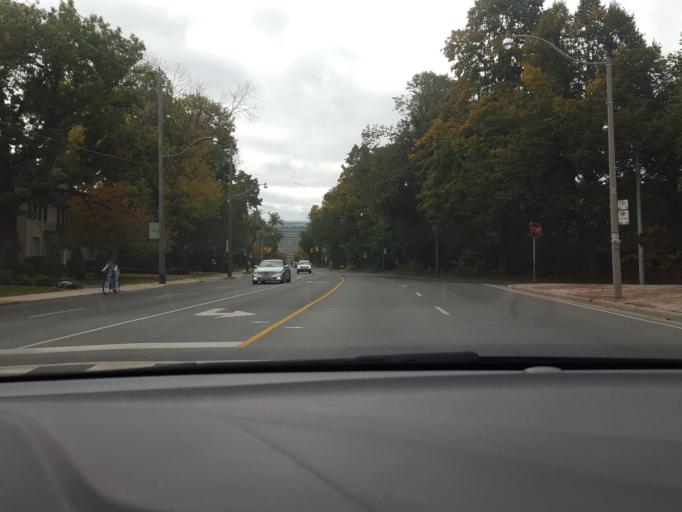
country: CA
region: Ontario
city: Toronto
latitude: 43.6954
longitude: -79.4024
